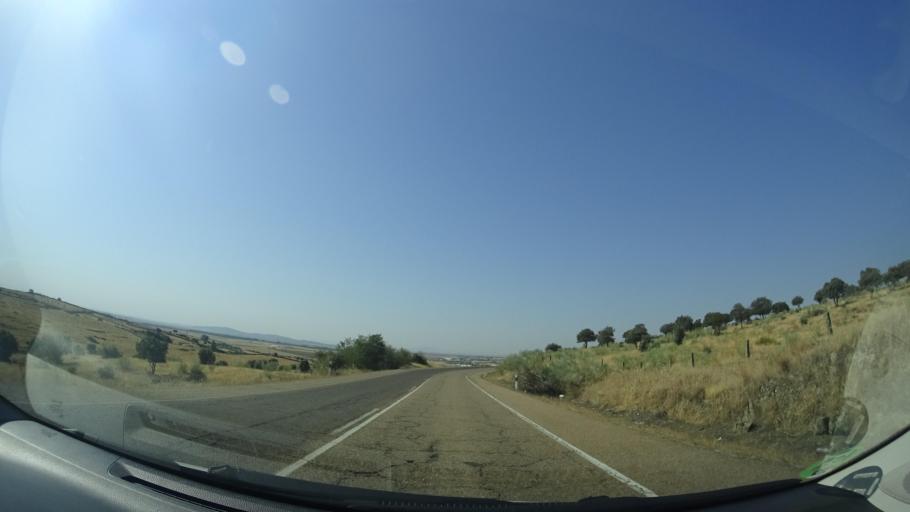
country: ES
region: Extremadura
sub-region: Provincia de Caceres
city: Escurial
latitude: 39.1691
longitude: -5.8978
